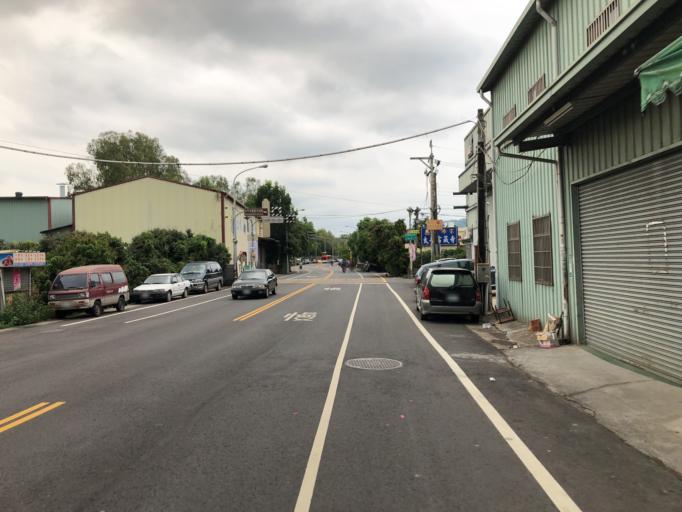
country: TW
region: Taiwan
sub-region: Taichung City
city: Taichung
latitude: 24.1146
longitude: 120.7322
